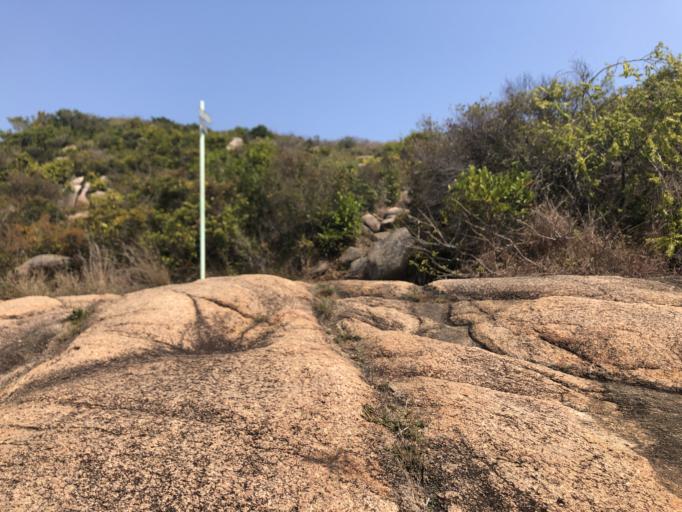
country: HK
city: Sok Kwu Wan
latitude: 22.1653
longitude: 114.2512
